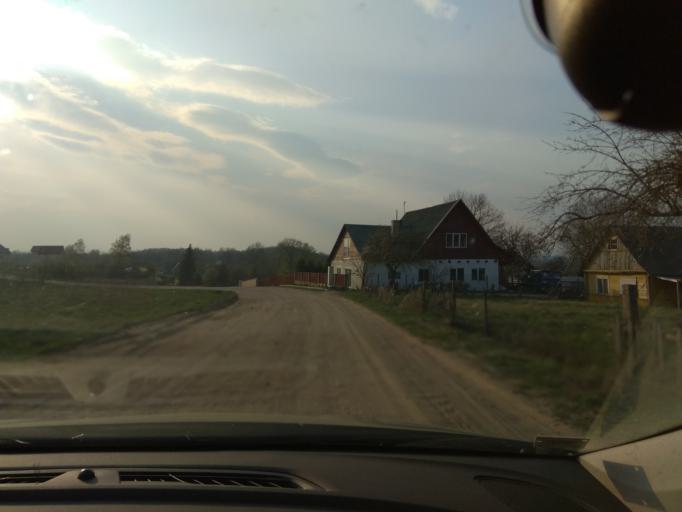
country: LT
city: Baltoji Voke
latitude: 54.5949
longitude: 25.1654
